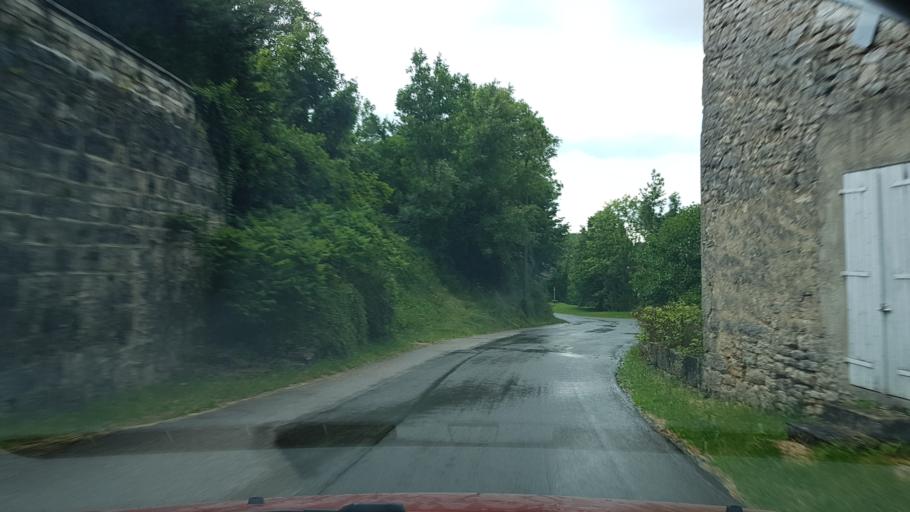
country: FR
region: Franche-Comte
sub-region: Departement du Jura
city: Clairvaux-les-Lacs
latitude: 46.5425
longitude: 5.7484
